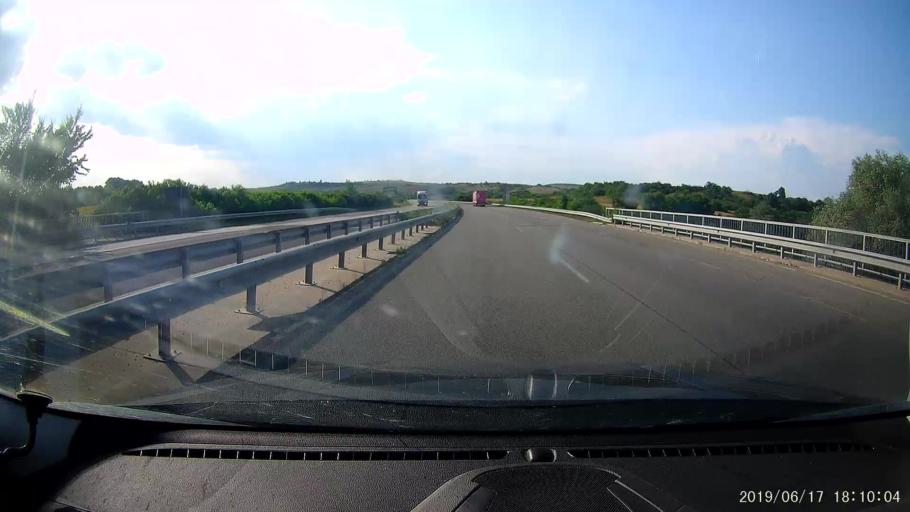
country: BG
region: Khaskovo
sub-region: Obshtina Lyubimets
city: Lyubimets
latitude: 41.8696
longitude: 26.0835
